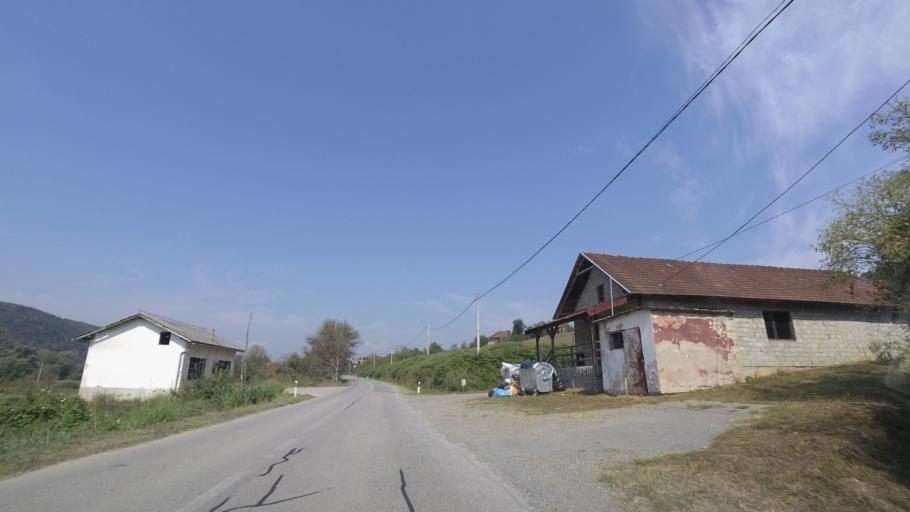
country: HR
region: Sisacko-Moslavacka
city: Dvor
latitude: 45.0866
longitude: 16.3114
